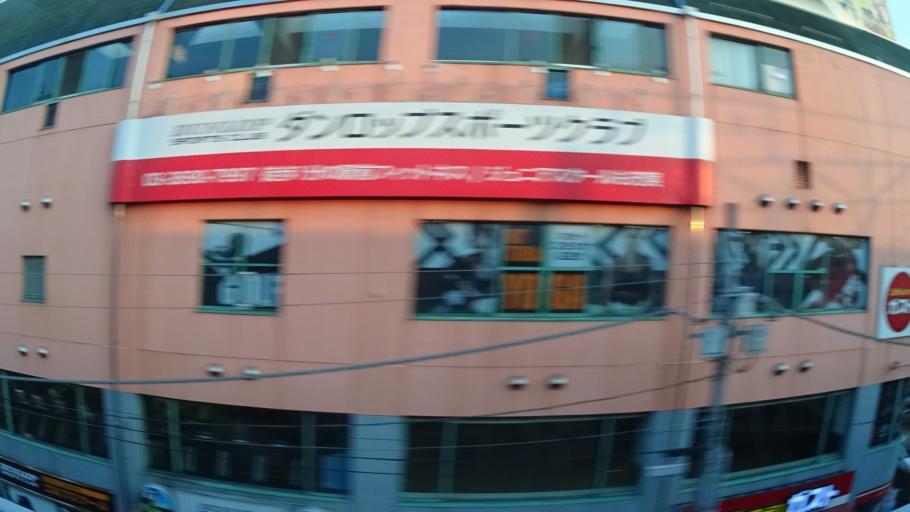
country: JP
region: Saitama
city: Soka
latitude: 35.7620
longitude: 139.8247
